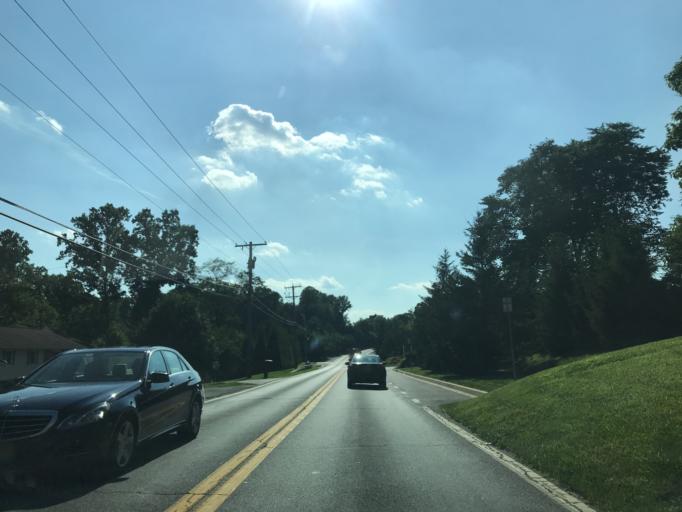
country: US
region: Maryland
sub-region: Baltimore County
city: Owings Mills
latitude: 39.4606
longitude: -76.7412
